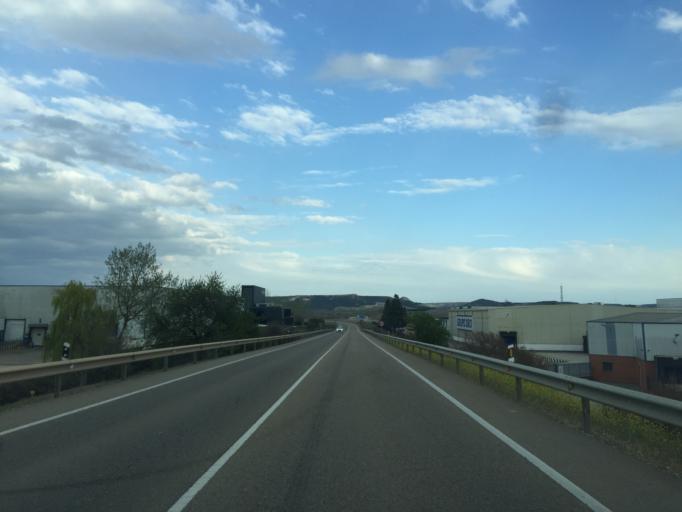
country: ES
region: Castille and Leon
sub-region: Provincia de Palencia
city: Venta de Banos
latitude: 41.9296
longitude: -4.4917
